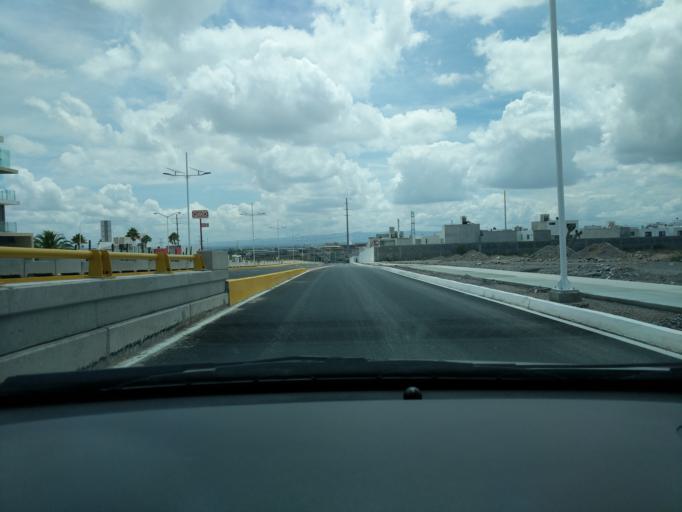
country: MX
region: San Luis Potosi
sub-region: Mexquitic de Carmona
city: Guadalupe Victoria
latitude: 22.1678
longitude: -101.0462
